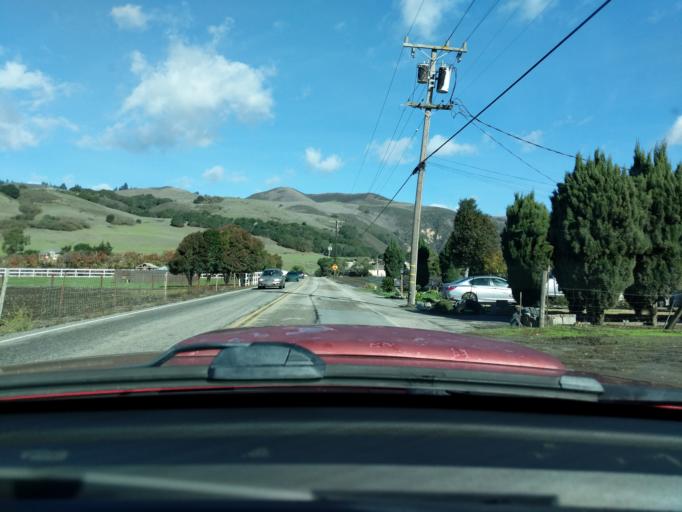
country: US
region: California
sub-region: San Benito County
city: Aromas
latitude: 36.9011
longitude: -121.6403
